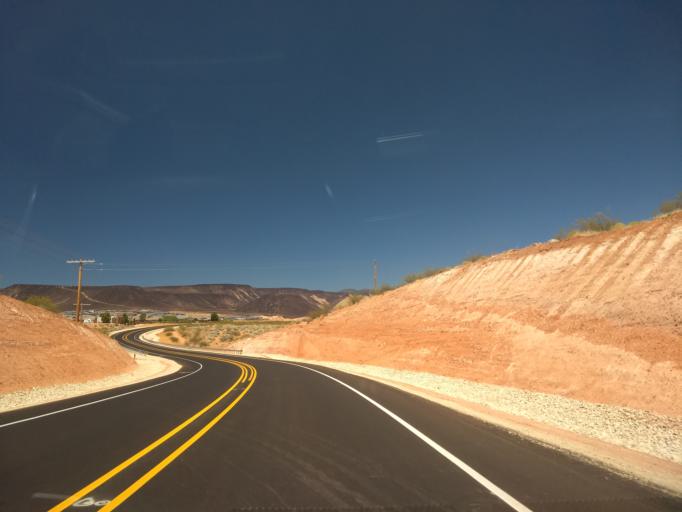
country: US
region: Utah
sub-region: Washington County
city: Washington
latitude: 37.1520
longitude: -113.5174
